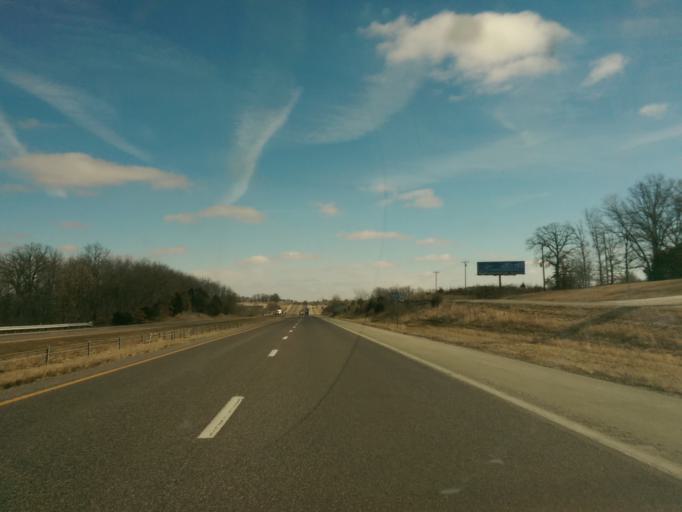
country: US
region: Missouri
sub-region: Callaway County
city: Fulton
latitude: 38.9442
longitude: -91.9341
